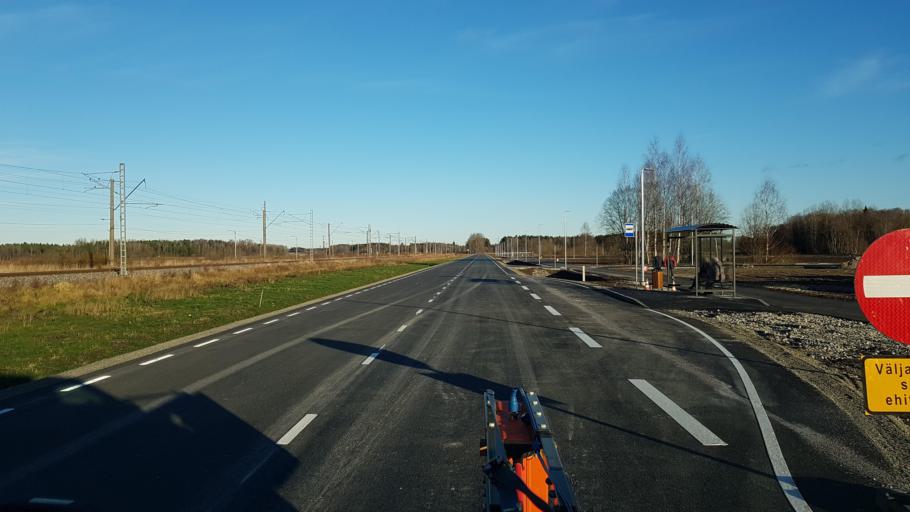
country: EE
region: Harju
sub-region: Saue linn
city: Saue
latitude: 59.3300
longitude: 24.5683
